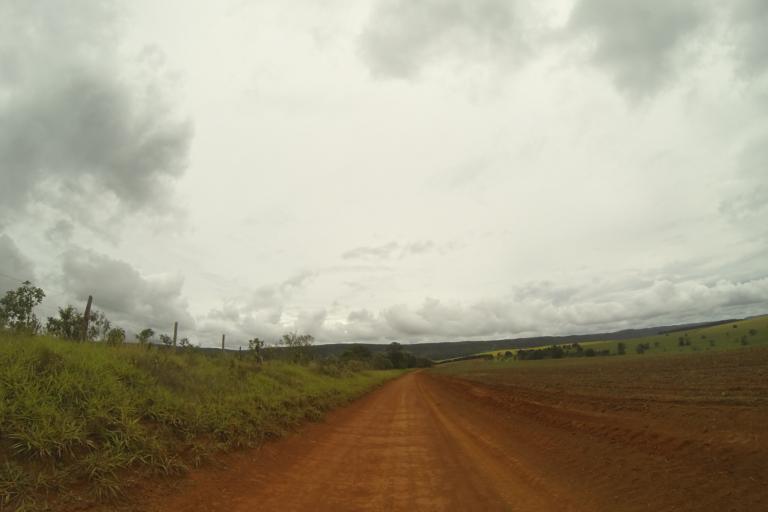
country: BR
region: Minas Gerais
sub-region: Ibia
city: Ibia
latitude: -19.7389
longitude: -46.6115
